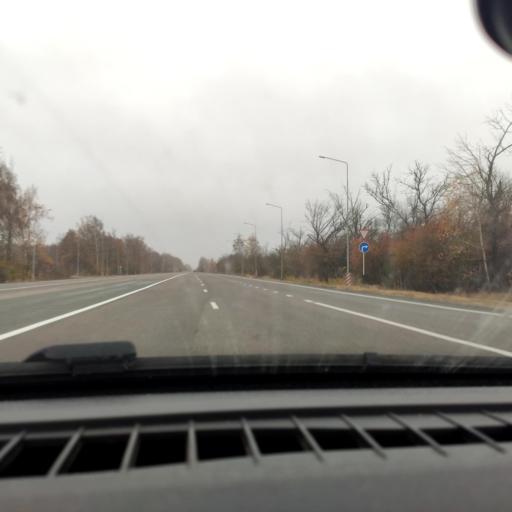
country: RU
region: Voronezj
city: Kolodeznyy
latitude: 51.3409
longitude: 39.0239
